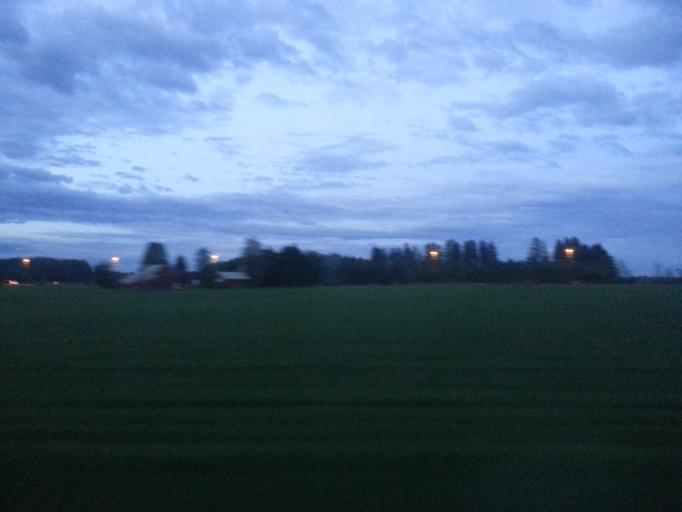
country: NO
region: Akershus
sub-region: Ullensaker
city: Klofta
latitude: 60.0557
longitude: 11.1389
